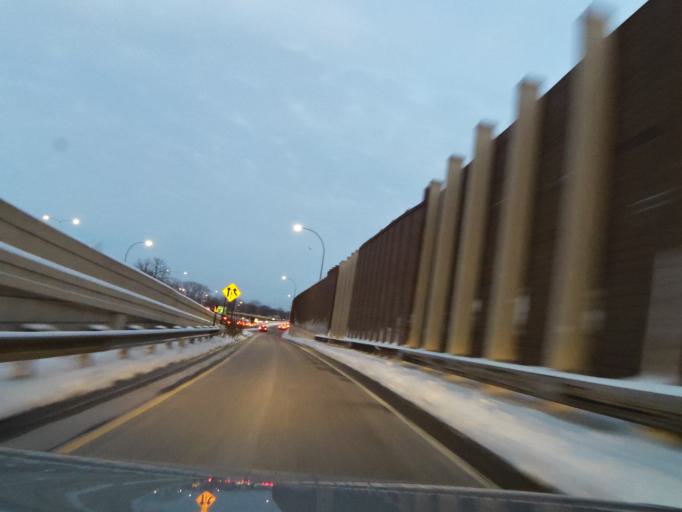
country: US
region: Minnesota
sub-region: Hennepin County
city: Richfield
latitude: 44.8902
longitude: -93.2724
